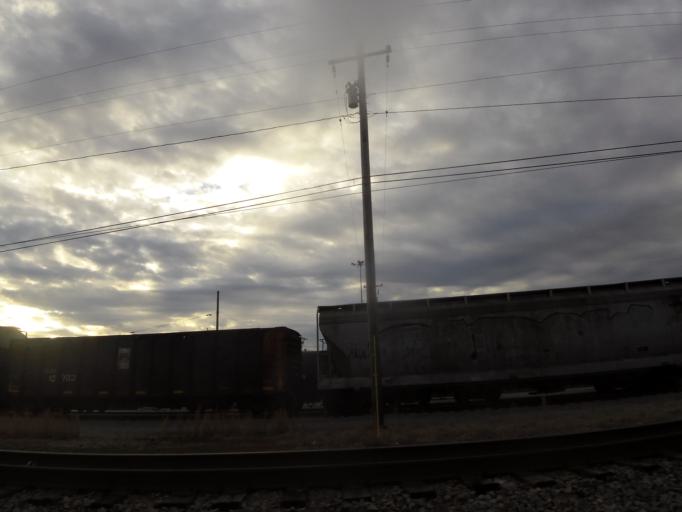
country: US
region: North Carolina
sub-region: Nash County
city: Rocky Mount
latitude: 35.9133
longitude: -77.8059
